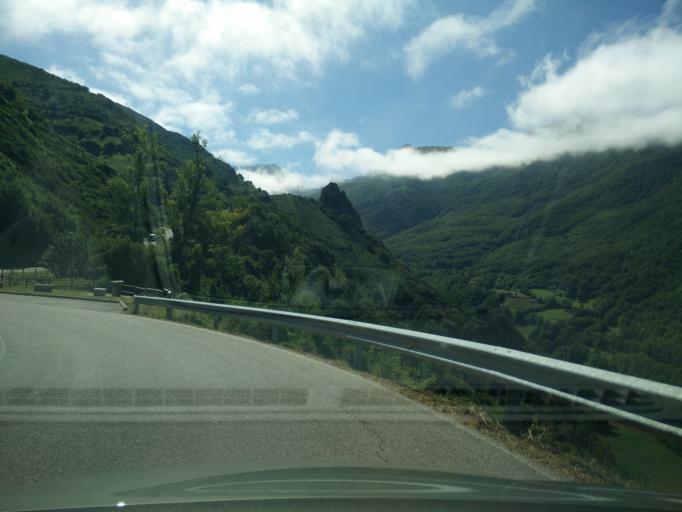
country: ES
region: Asturias
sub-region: Province of Asturias
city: Pola de Somiedo
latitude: 43.0830
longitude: -6.2327
